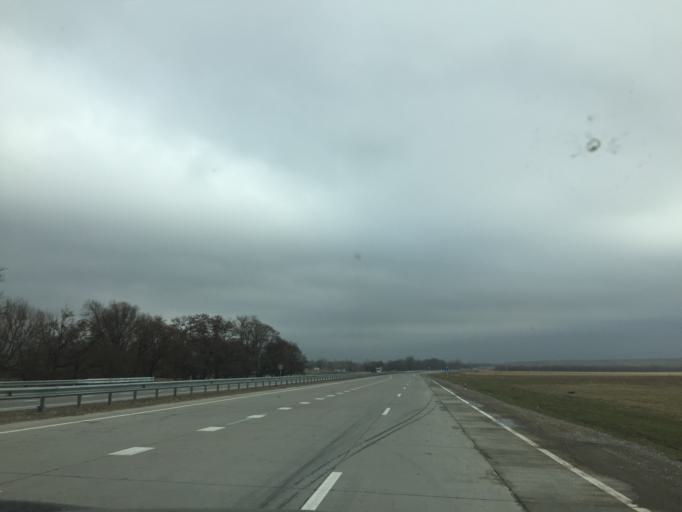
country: KZ
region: Ongtustik Qazaqstan
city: Kokterek
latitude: 42.5549
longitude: 70.1406
